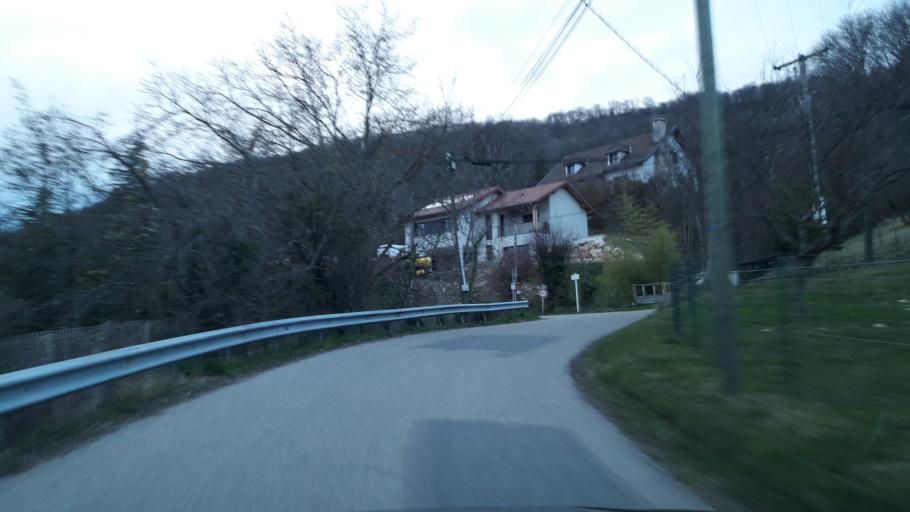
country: FR
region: Rhone-Alpes
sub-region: Departement de l'Isere
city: Herbeys
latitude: 45.1466
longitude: 5.7908
